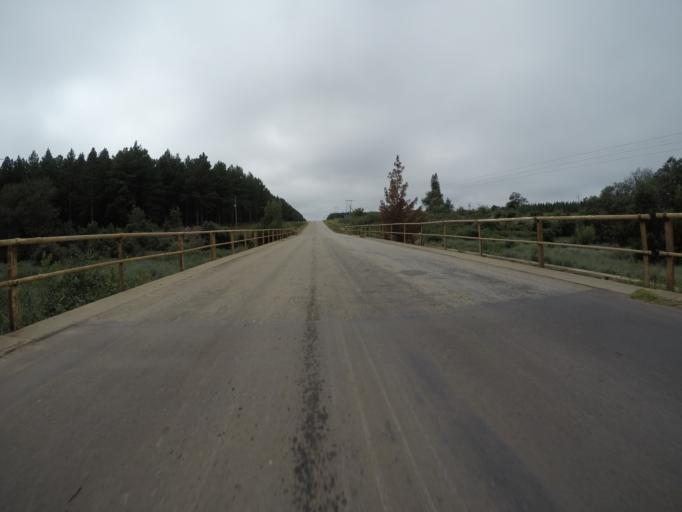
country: ZA
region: Eastern Cape
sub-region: Cacadu District Municipality
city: Kareedouw
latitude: -33.9948
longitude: 24.1230
